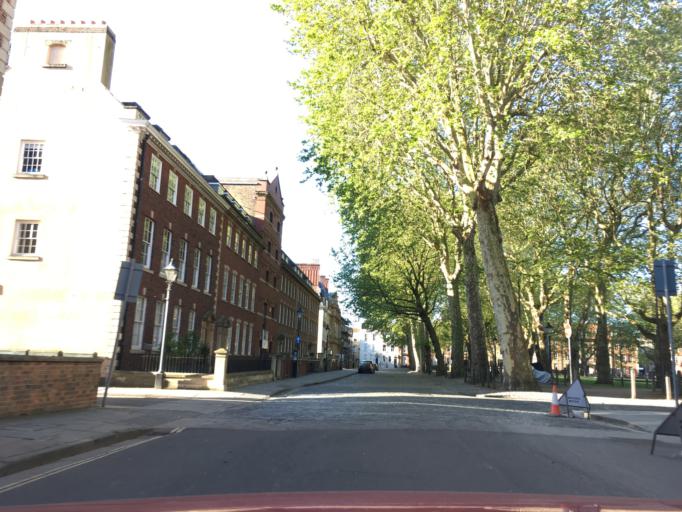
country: GB
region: England
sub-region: Bristol
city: Bristol
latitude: 51.4513
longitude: -2.5934
